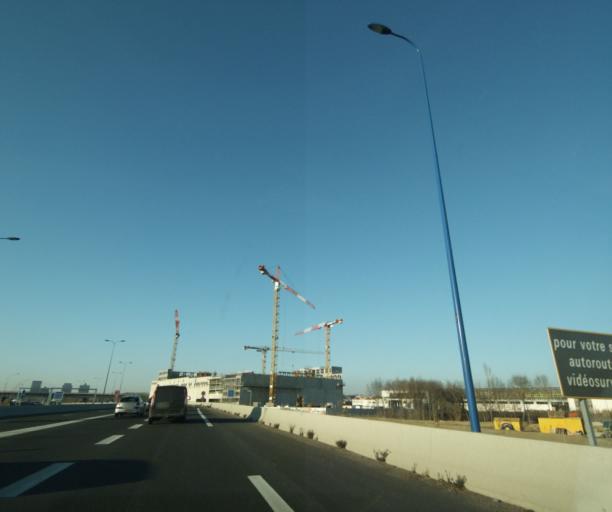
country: FR
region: Midi-Pyrenees
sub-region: Departement de la Haute-Garonne
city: Ramonville-Saint-Agne
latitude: 43.5609
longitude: 1.4893
